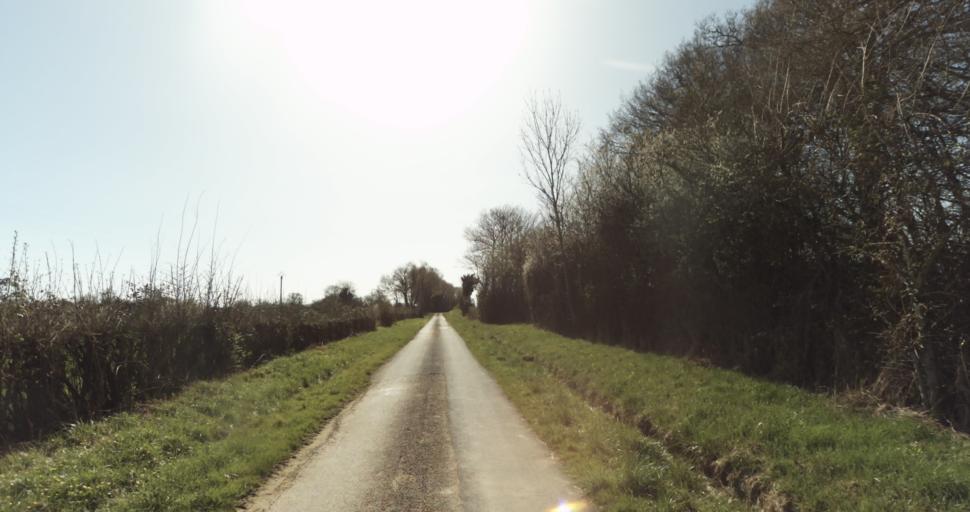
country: FR
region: Lower Normandy
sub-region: Departement du Calvados
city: Saint-Pierre-sur-Dives
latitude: 48.9492
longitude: 0.0022
